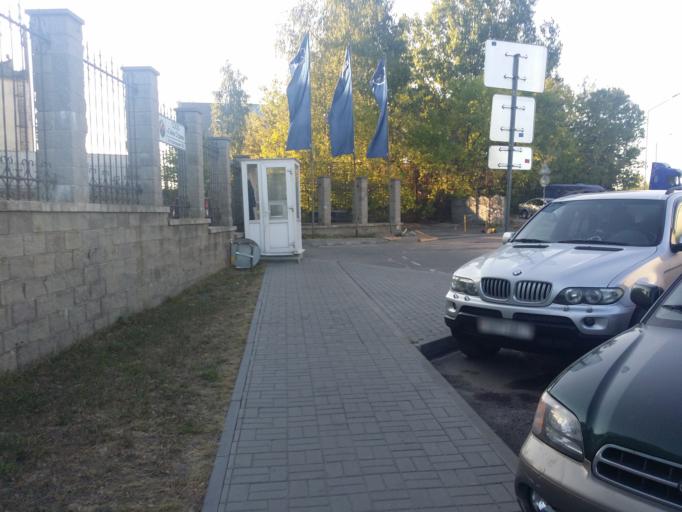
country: BY
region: Minsk
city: Vyaliki Trastsyanets
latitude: 53.8517
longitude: 27.6953
